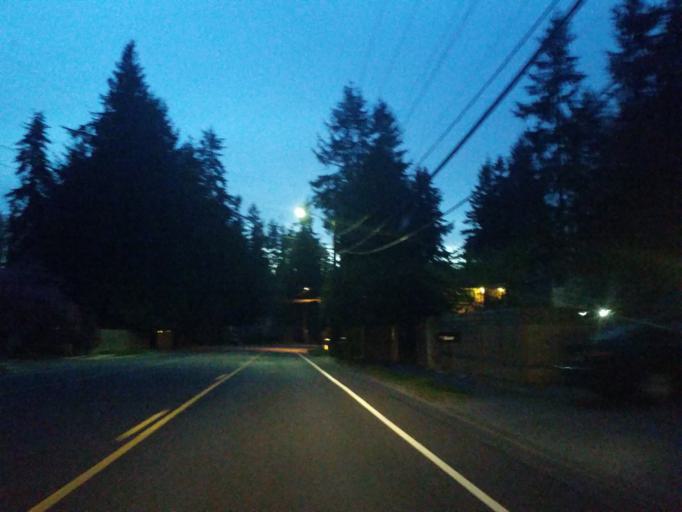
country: US
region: Washington
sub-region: Snohomish County
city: Esperance
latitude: 47.7786
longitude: -122.3630
